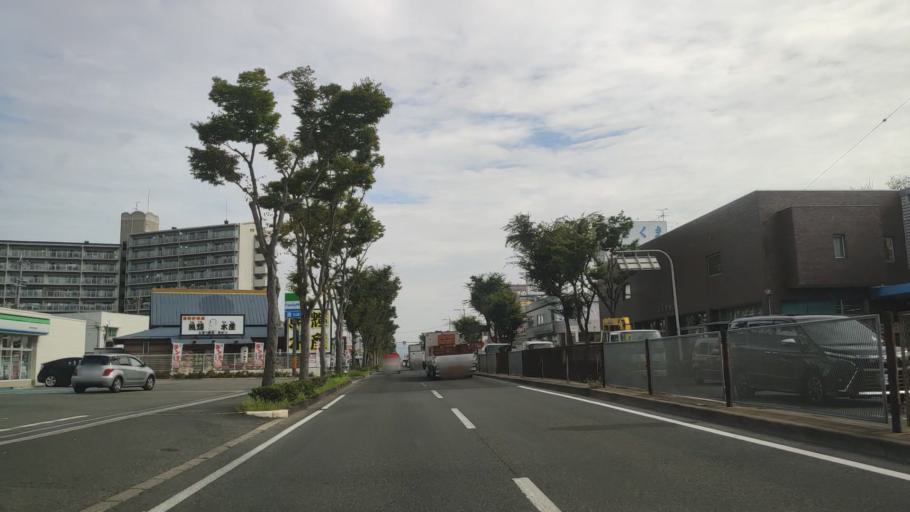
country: JP
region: Osaka
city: Tondabayashicho
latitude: 34.5091
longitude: 135.6012
